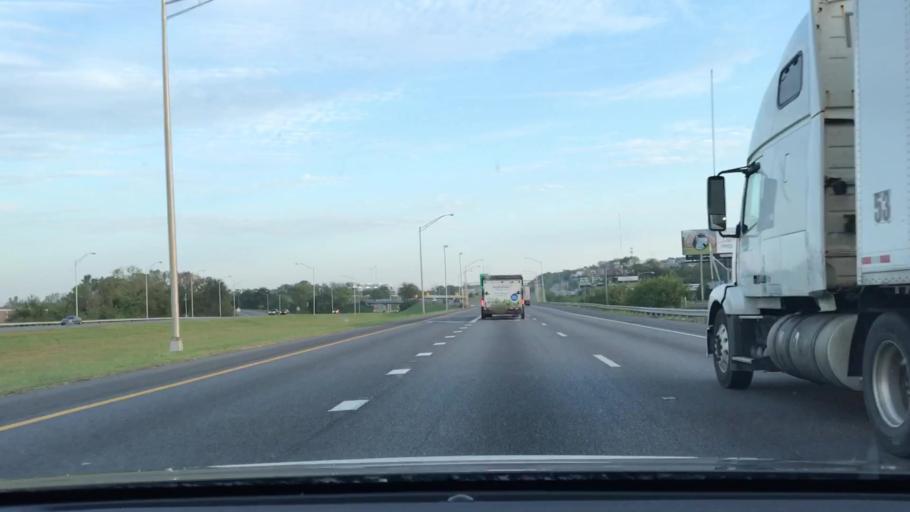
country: US
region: Tennessee
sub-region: Davidson County
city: Nashville
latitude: 36.1863
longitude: -86.7752
